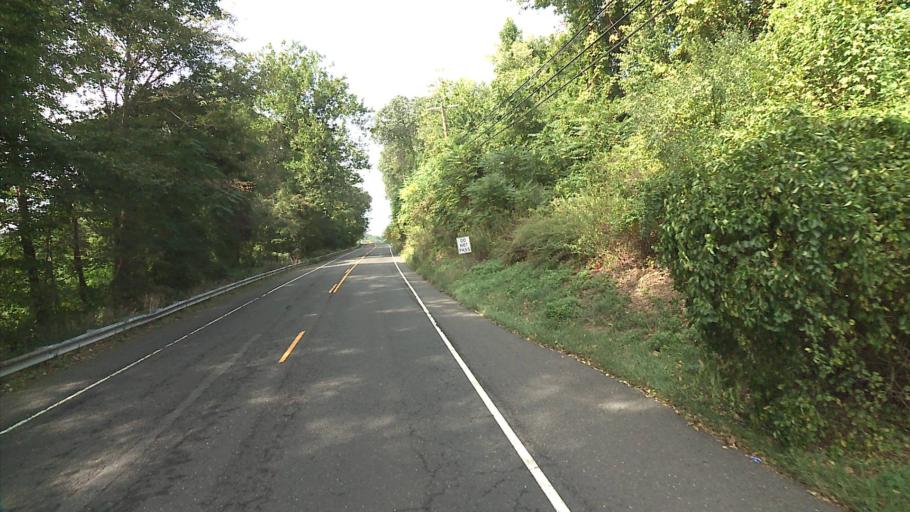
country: US
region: Connecticut
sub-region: New Haven County
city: Oxford
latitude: 41.3845
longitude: -73.1671
